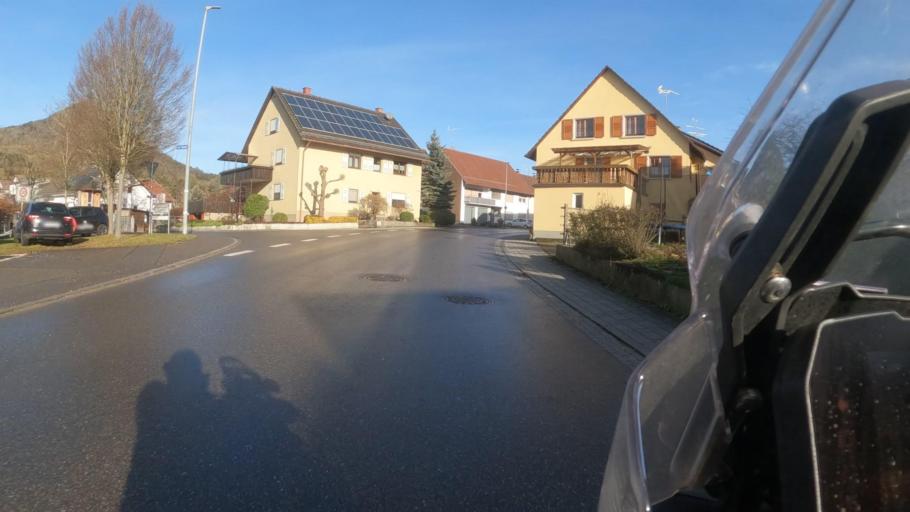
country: DE
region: Baden-Wuerttemberg
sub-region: Freiburg Region
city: Neuhausen
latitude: 47.8225
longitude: 8.7571
